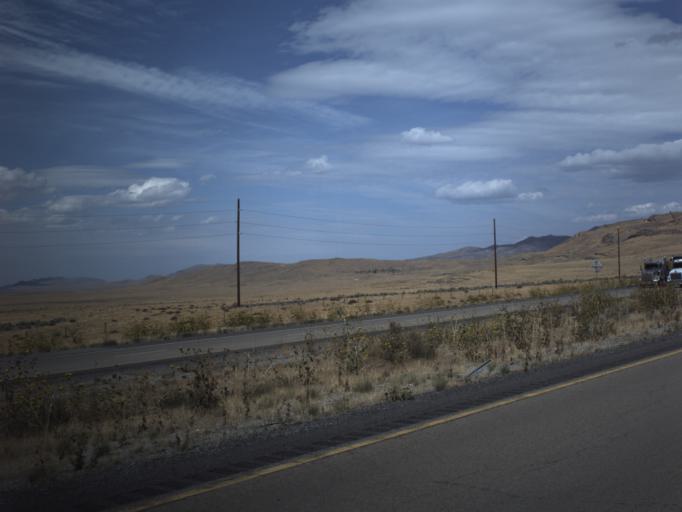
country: US
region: Utah
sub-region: Tooele County
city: Grantsville
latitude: 40.8130
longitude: -112.9237
